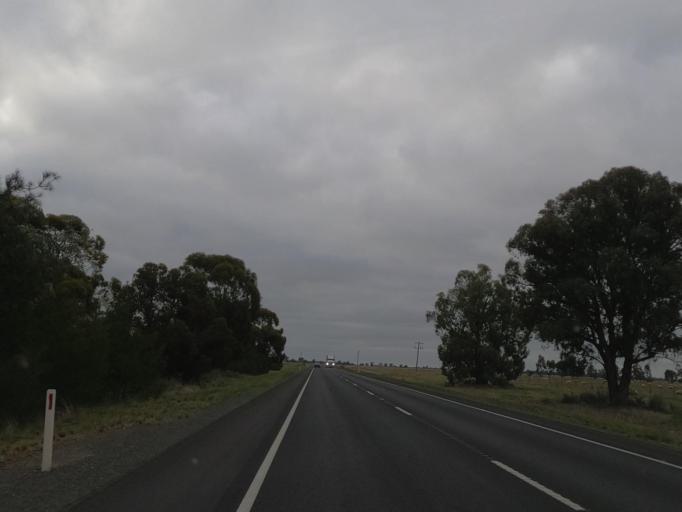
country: AU
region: Victoria
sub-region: Greater Bendigo
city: Long Gully
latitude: -36.3025
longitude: 143.9749
